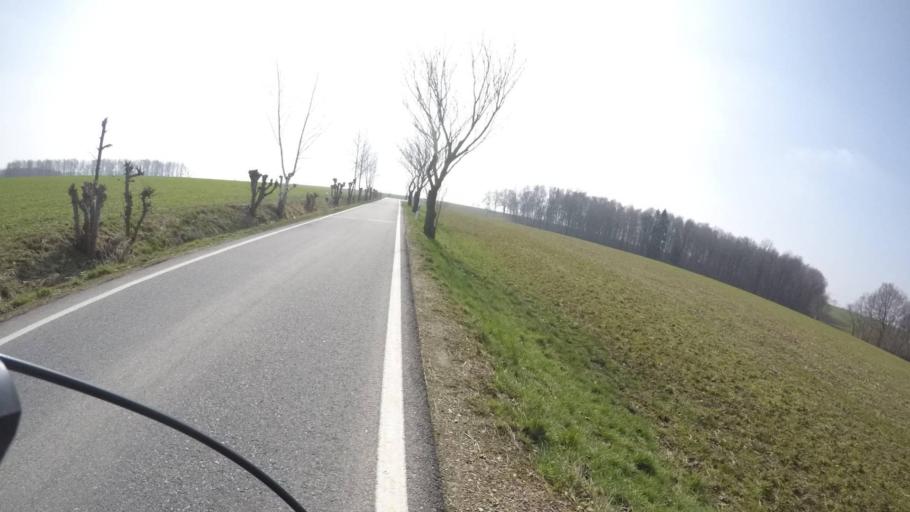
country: DE
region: Saxony
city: Niederfrohna
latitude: 50.8637
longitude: 12.6913
